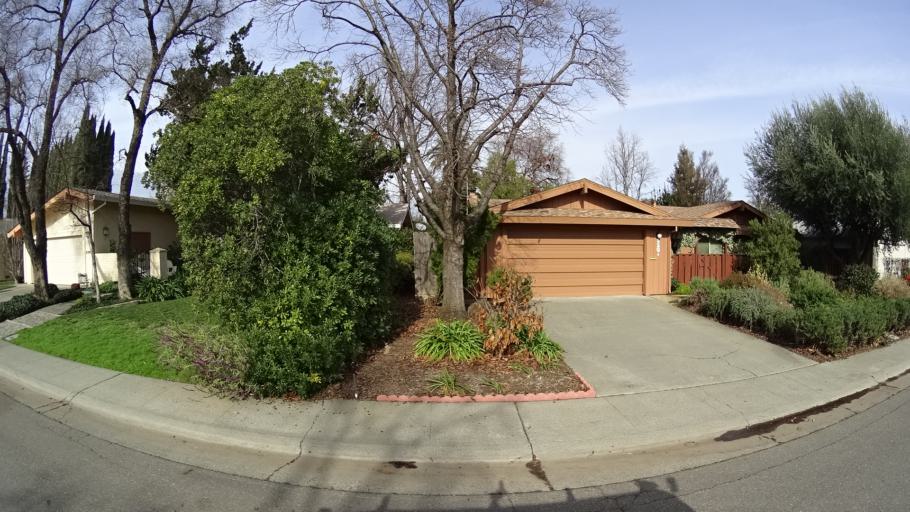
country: US
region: California
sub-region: Yolo County
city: Davis
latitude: 38.5487
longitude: -121.6863
